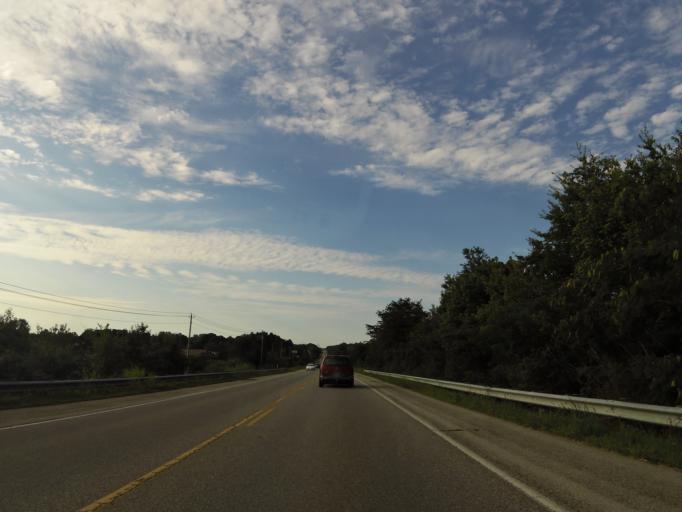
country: US
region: Tennessee
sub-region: Monroe County
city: Vonore
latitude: 35.5994
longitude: -84.2734
